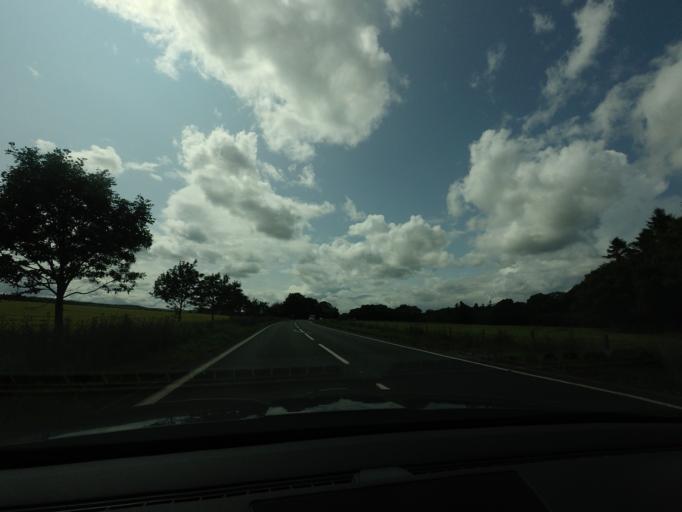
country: GB
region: Scotland
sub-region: Moray
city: Forres
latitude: 57.5935
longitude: -3.6985
